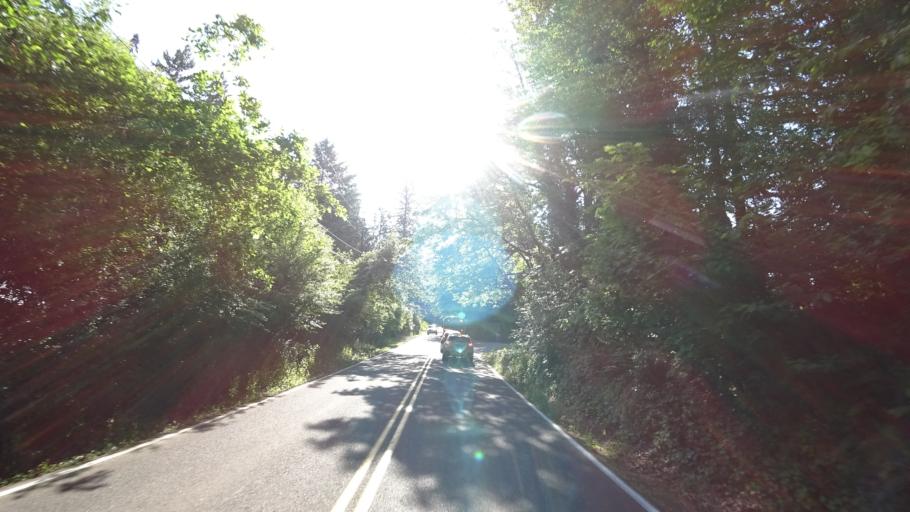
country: US
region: Oregon
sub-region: Washington County
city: West Slope
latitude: 45.4979
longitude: -122.7335
